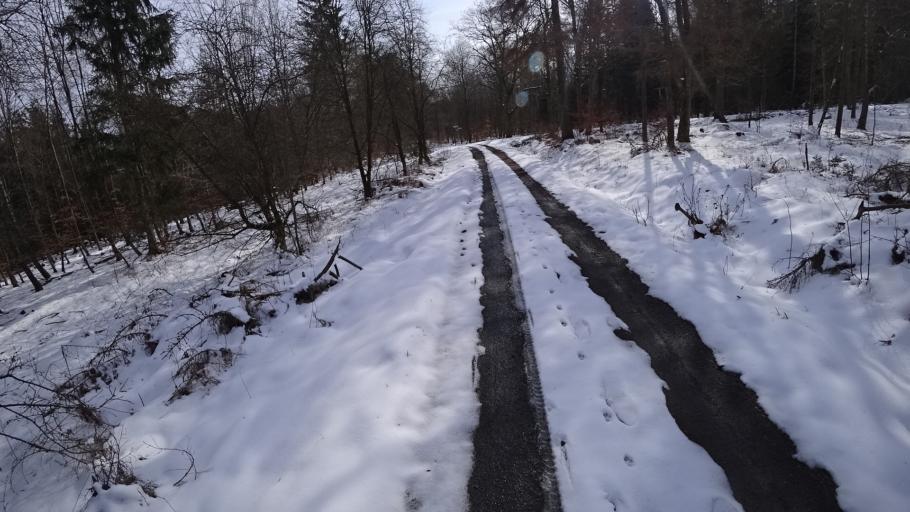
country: DE
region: Rheinland-Pfalz
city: Morlen
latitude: 50.6835
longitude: 7.8763
